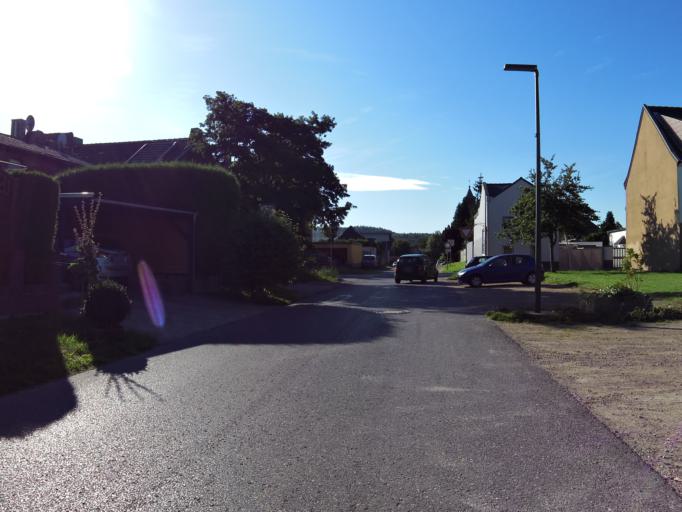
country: DE
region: North Rhine-Westphalia
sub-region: Regierungsbezirk Koln
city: Alsdorf
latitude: 50.8788
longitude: 6.1772
